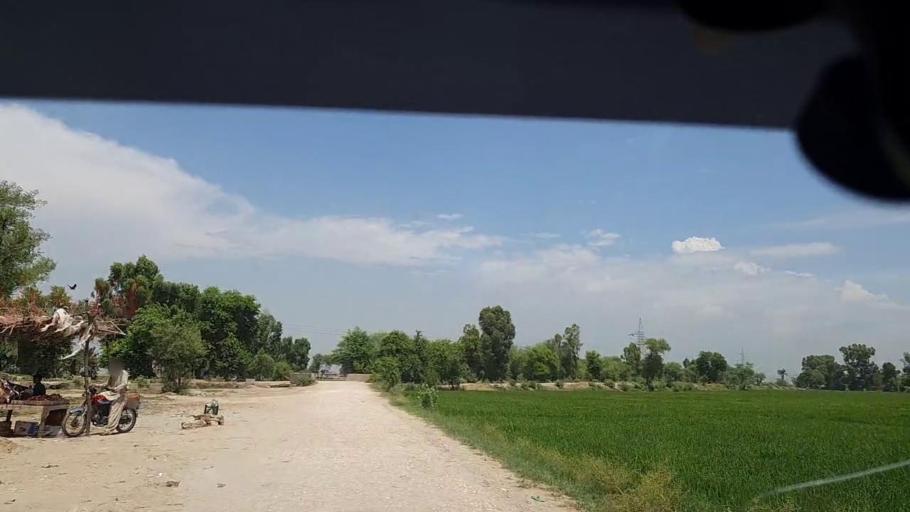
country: PK
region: Sindh
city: Ghauspur
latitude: 28.1029
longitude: 68.9860
